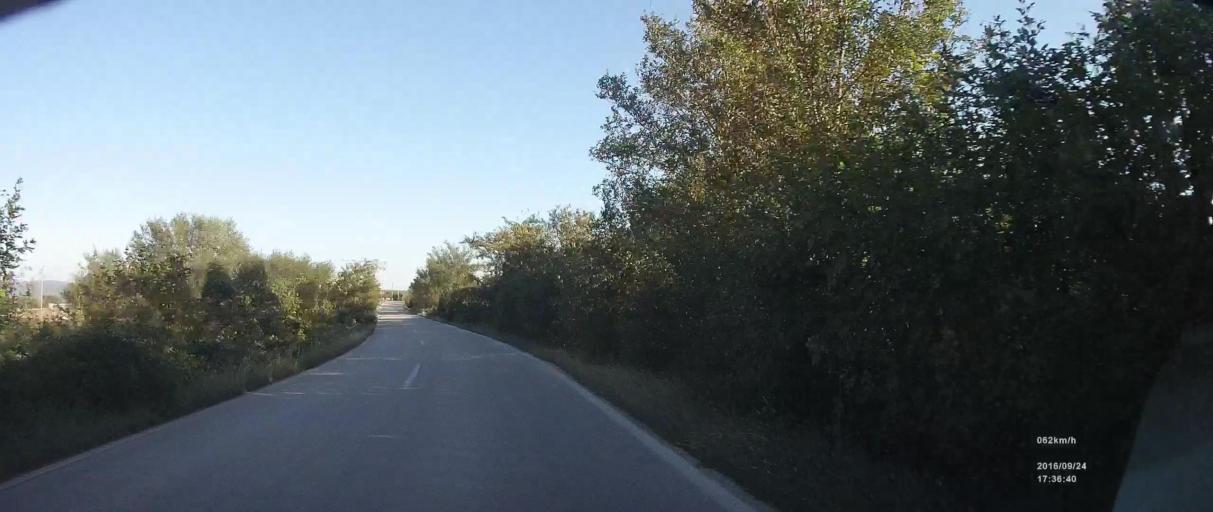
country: HR
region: Zadarska
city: Posedarje
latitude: 44.1534
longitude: 15.4777
